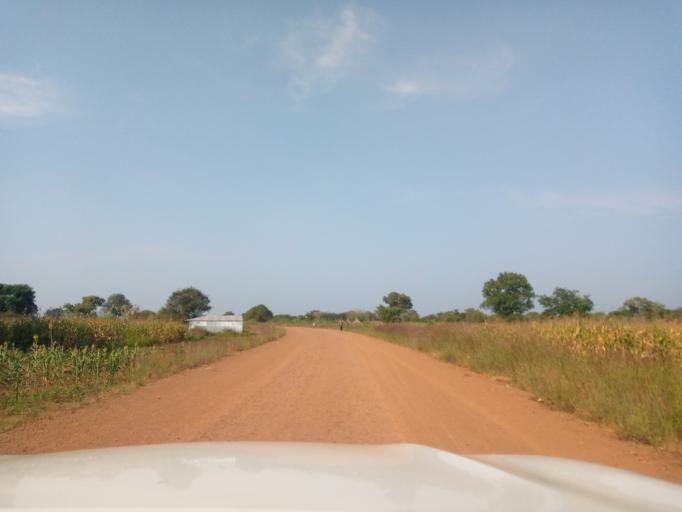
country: ET
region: Oromiya
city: Mendi
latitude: 10.1443
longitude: 34.9525
